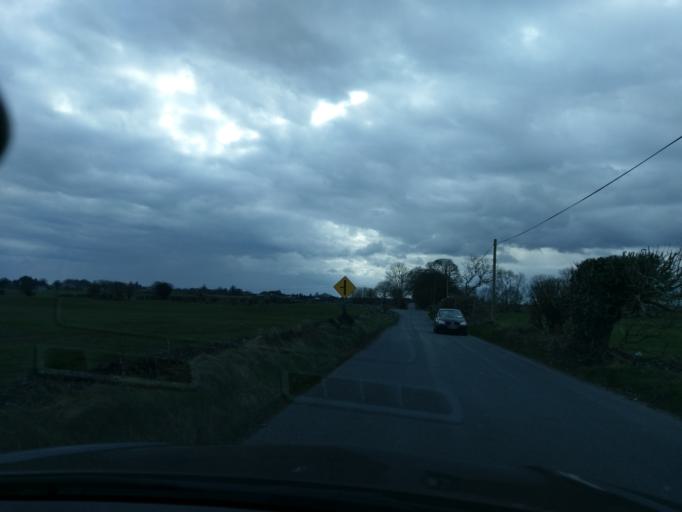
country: IE
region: Connaught
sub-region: County Galway
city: Athenry
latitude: 53.4766
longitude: -8.6444
